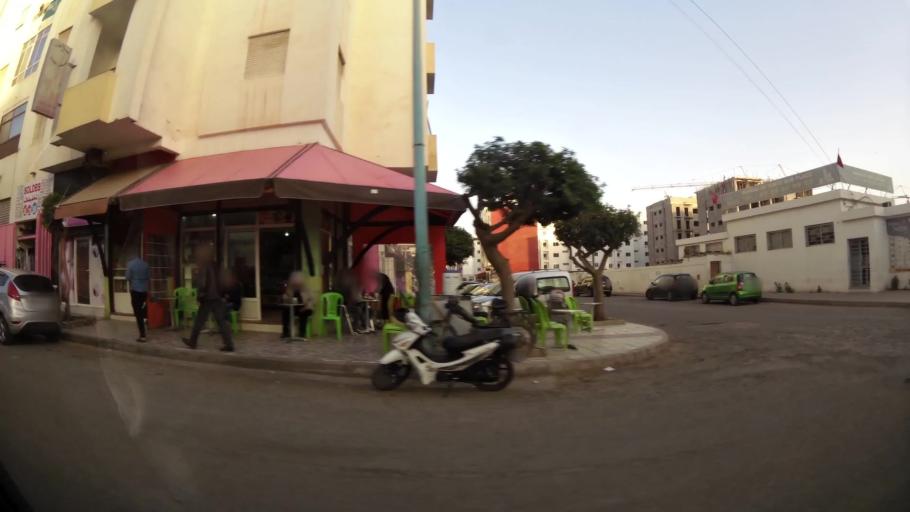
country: MA
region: Oued ed Dahab-Lagouira
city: Dakhla
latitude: 30.3981
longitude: -9.5519
